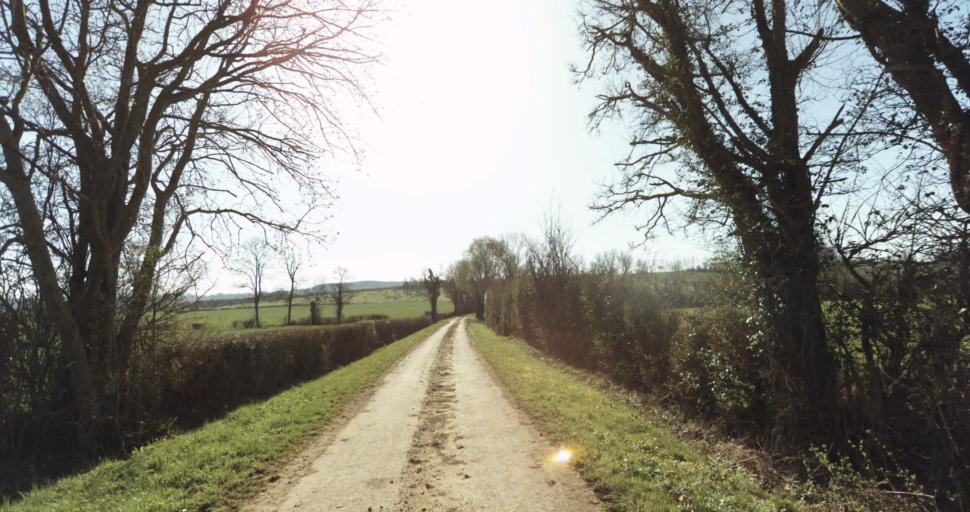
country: FR
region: Lower Normandy
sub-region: Departement du Calvados
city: Saint-Pierre-sur-Dives
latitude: 48.9528
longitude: 0.0212
